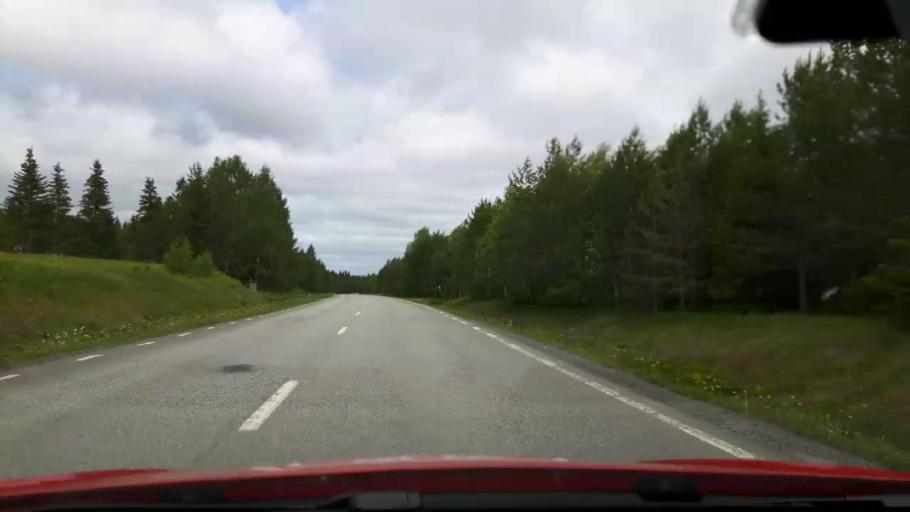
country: SE
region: Jaemtland
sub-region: Krokoms Kommun
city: Krokom
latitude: 63.3702
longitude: 14.5076
